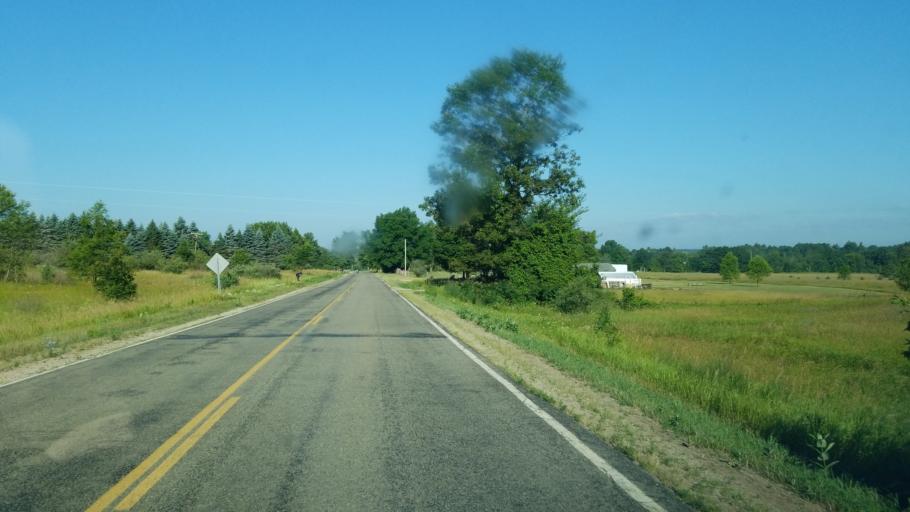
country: US
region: Michigan
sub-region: Montcalm County
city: Howard City
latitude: 43.4903
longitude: -85.4221
